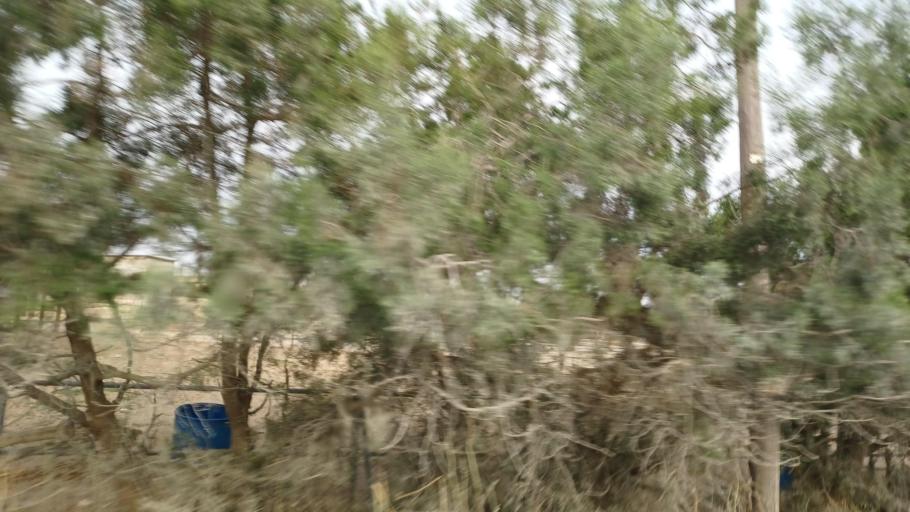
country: CY
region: Ammochostos
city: Achna
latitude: 35.0409
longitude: 33.7906
